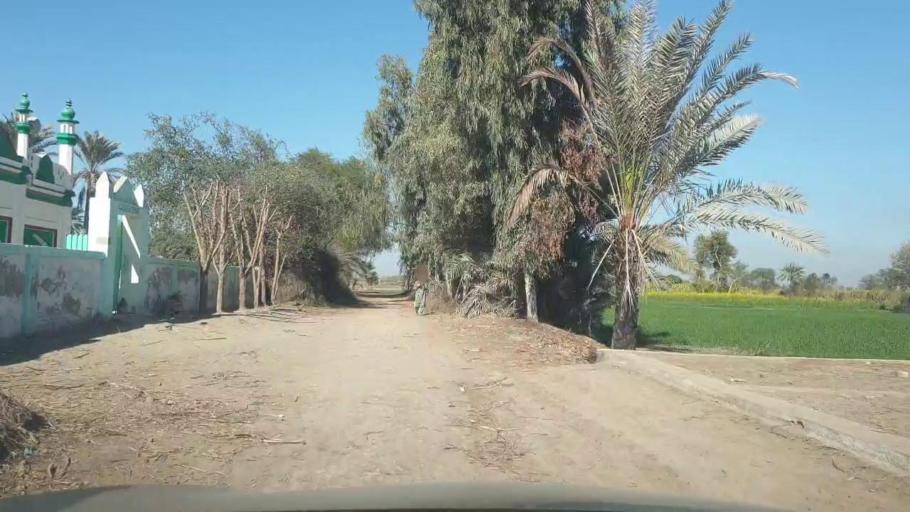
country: PK
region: Sindh
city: Mirpur Mathelo
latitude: 28.0821
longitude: 69.4894
